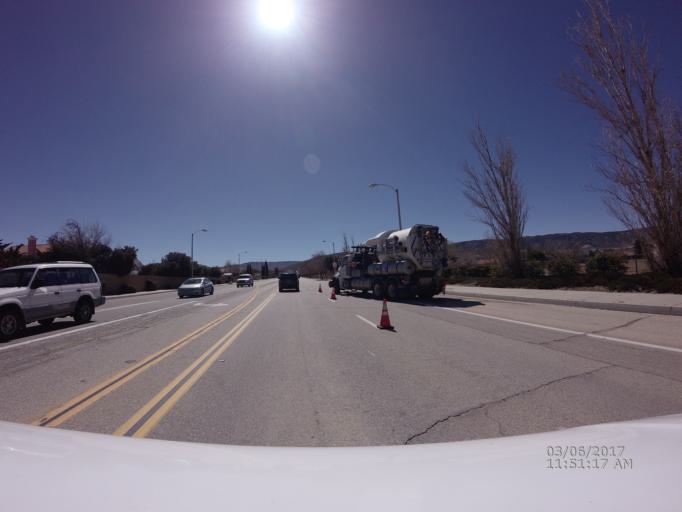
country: US
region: California
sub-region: Los Angeles County
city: Quartz Hill
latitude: 34.6525
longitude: -118.2363
